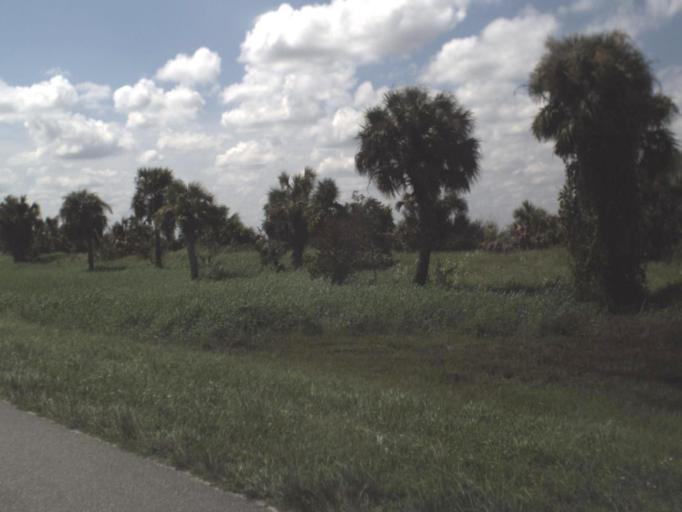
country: US
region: Florida
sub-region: Hendry County
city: Port LaBelle
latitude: 26.5900
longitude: -81.4367
